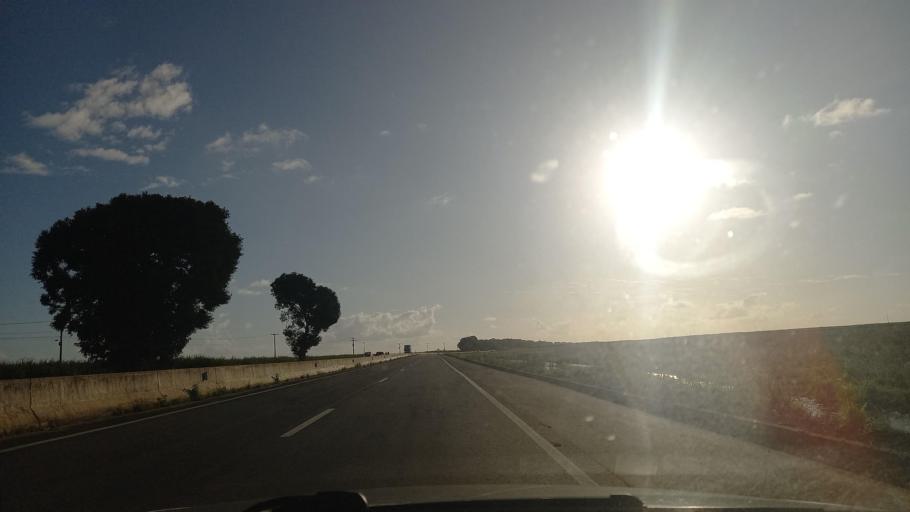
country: BR
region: Alagoas
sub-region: Campo Alegre
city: Campo Alegre
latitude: -9.8009
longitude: -36.2824
